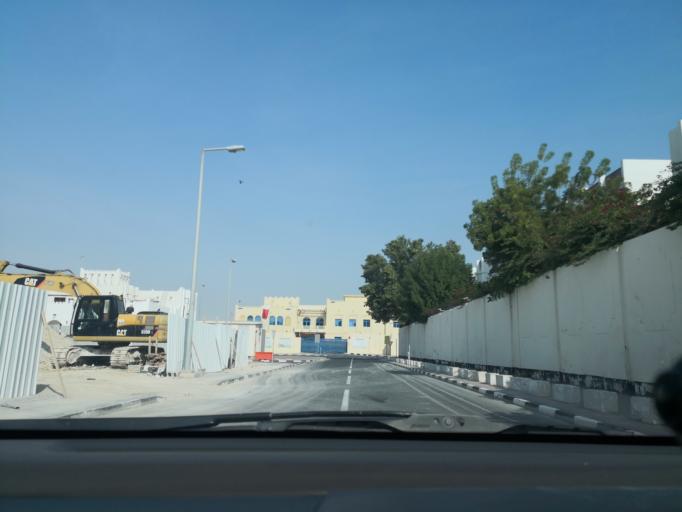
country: QA
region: Baladiyat ad Dawhah
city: Doha
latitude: 25.3274
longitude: 51.5114
